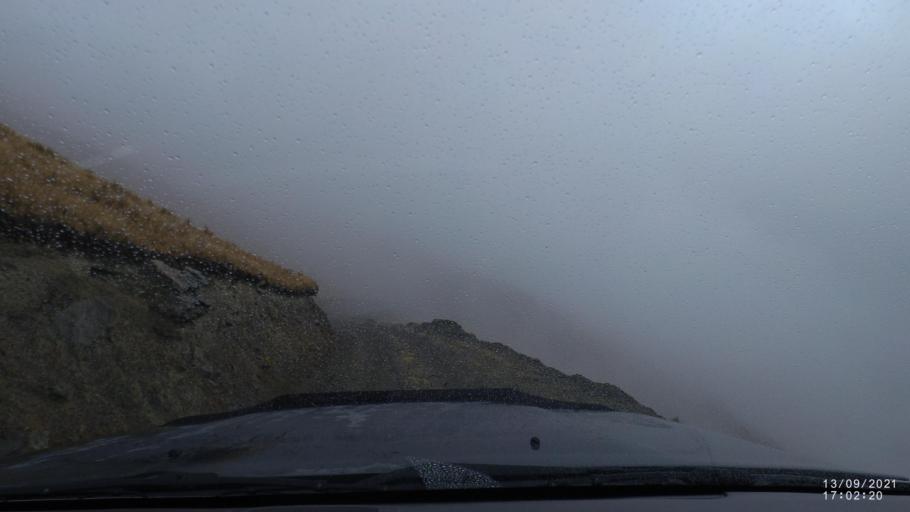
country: BO
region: Cochabamba
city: Colomi
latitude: -17.3174
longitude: -65.7222
